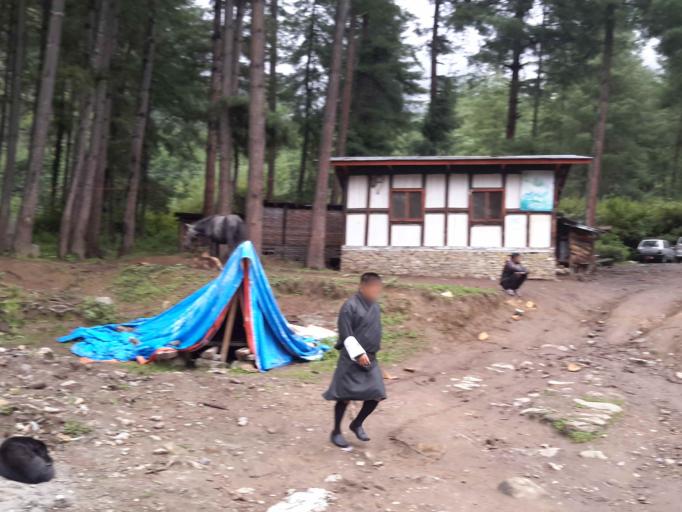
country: BT
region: Paro
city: Paro
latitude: 27.4814
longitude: 89.3609
